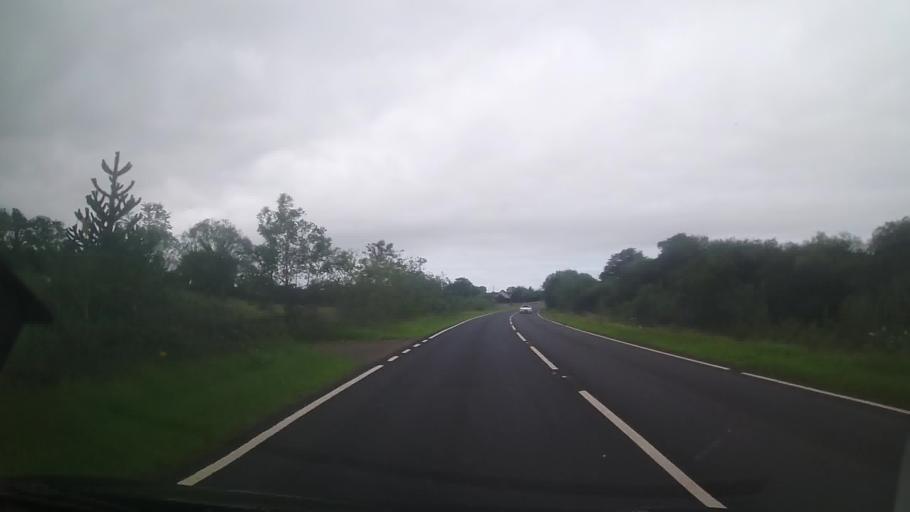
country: GB
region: Wales
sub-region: Gwynedd
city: Caernarfon
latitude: 53.1643
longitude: -4.3154
